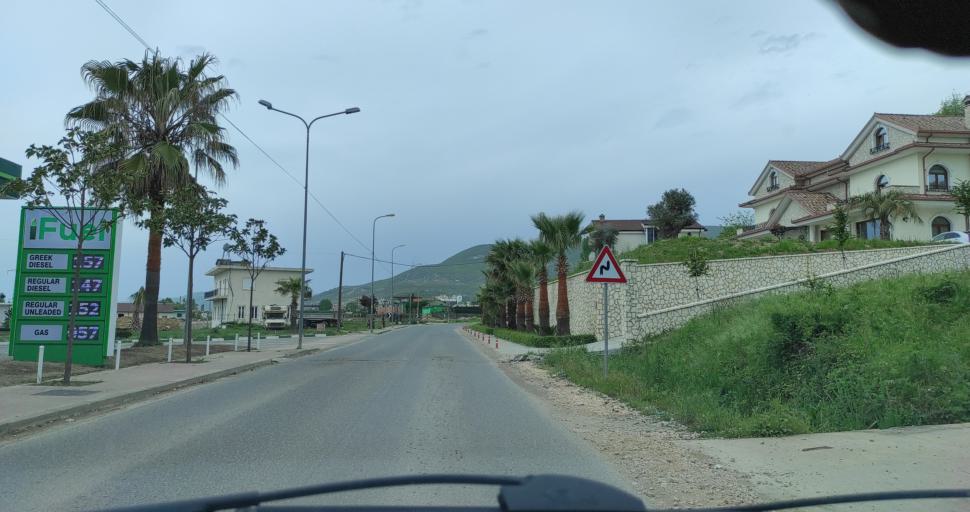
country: AL
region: Lezhe
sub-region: Rrethi i Kurbinit
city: Lac
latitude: 41.6246
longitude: 19.7087
